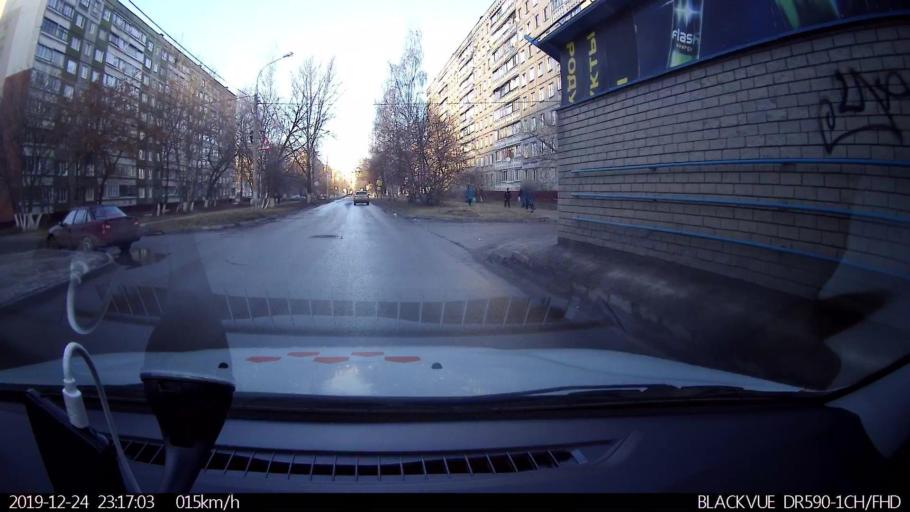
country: RU
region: Nizjnij Novgorod
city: Gorbatovka
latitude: 56.2530
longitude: 43.8583
